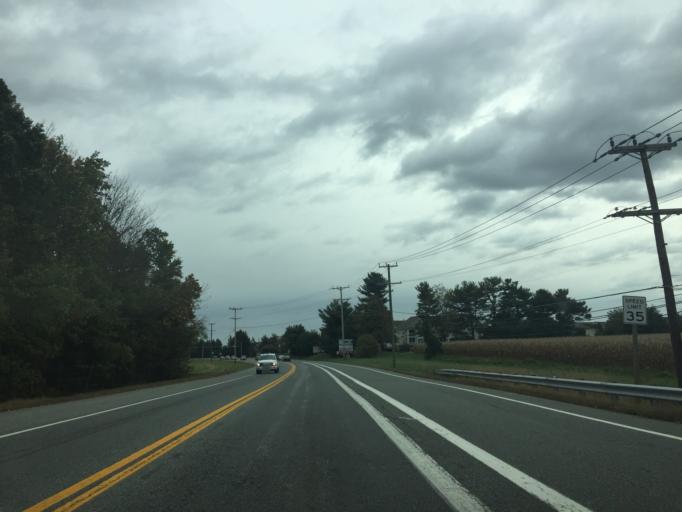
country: US
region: Maryland
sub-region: Harford County
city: Havre de Grace
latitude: 39.5643
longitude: -76.1243
